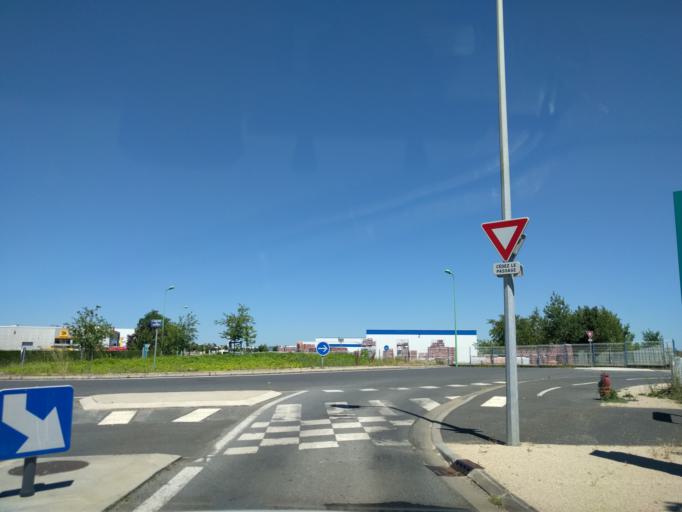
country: FR
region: Poitou-Charentes
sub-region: Departement des Deux-Sevres
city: Aiffres
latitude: 46.3303
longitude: -0.4098
